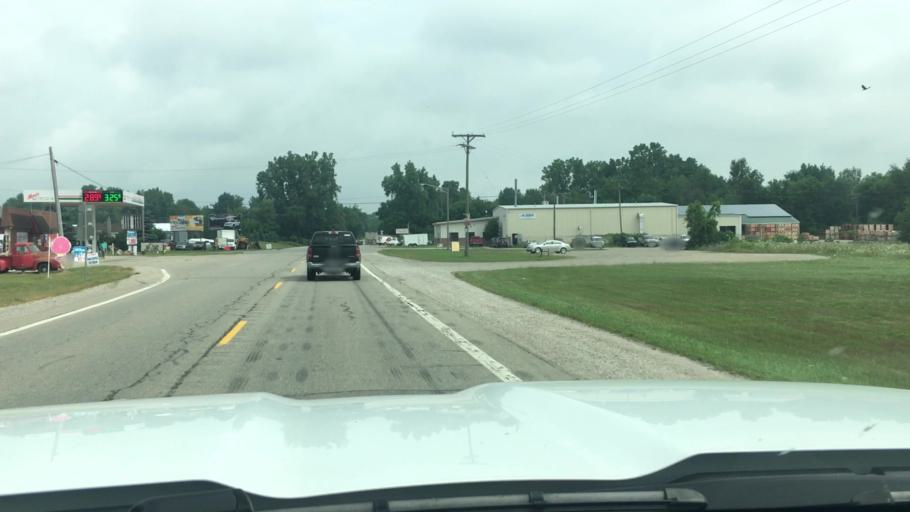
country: US
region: Michigan
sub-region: Sanilac County
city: Brown City
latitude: 43.1516
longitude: -83.0751
